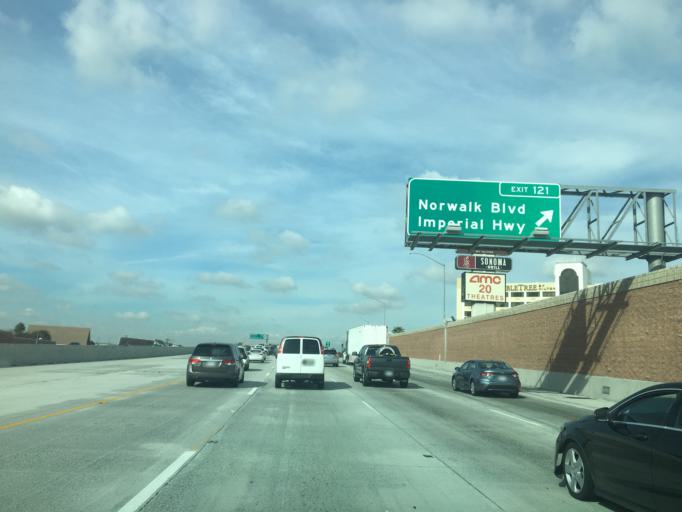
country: US
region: California
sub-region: Los Angeles County
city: Norwalk
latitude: 33.9102
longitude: -118.0702
